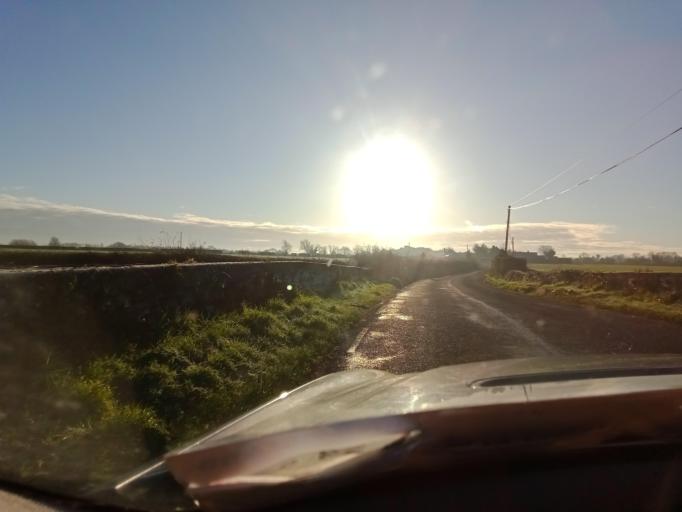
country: IE
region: Leinster
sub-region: Kilkenny
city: Callan
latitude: 52.5338
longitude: -7.3859
